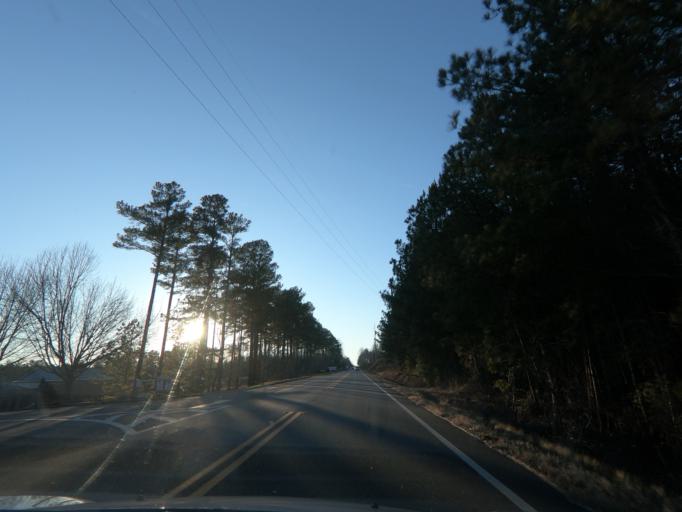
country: US
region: Georgia
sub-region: Dawson County
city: Dawsonville
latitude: 34.3539
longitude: -84.0807
